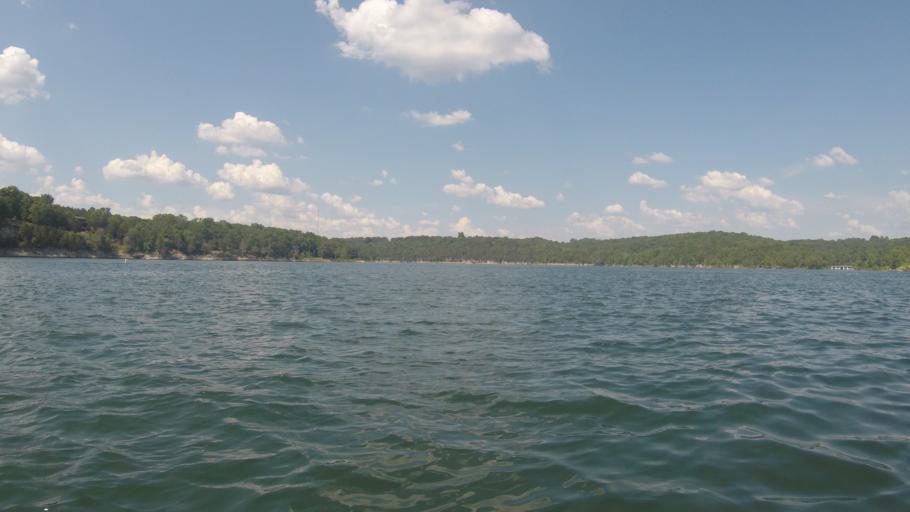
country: US
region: Missouri
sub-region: Barry County
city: Shell Knob
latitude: 36.5646
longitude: -93.5971
